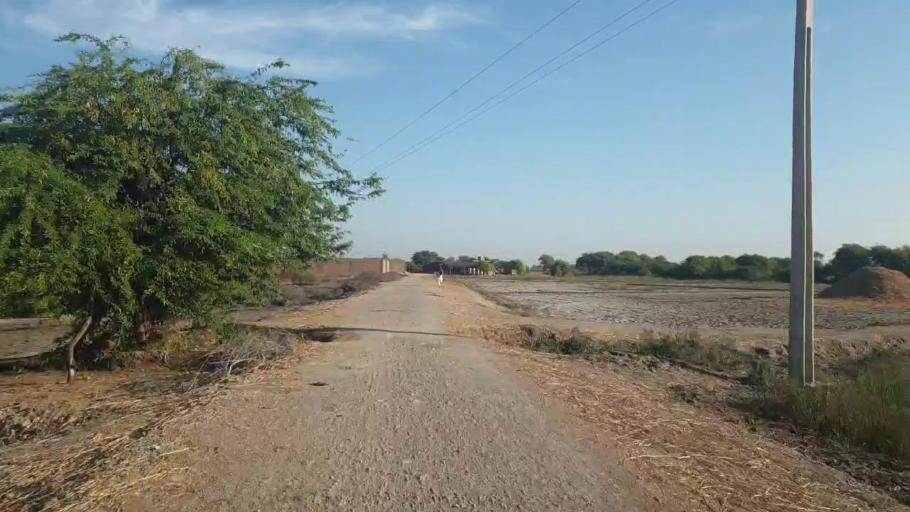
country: PK
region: Sindh
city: Talhar
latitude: 24.8151
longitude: 68.8394
